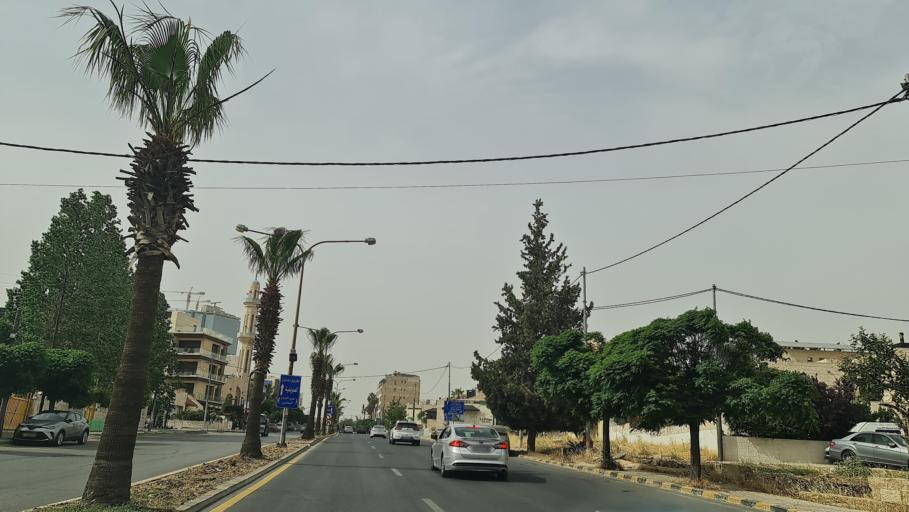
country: JO
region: Amman
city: Wadi as Sir
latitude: 31.9533
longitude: 35.8706
